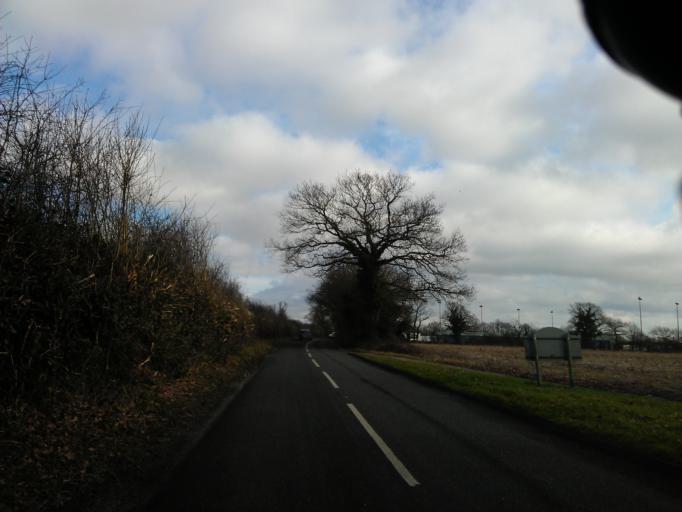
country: GB
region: England
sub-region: Essex
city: Wivenhoe
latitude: 51.8732
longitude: 0.9663
